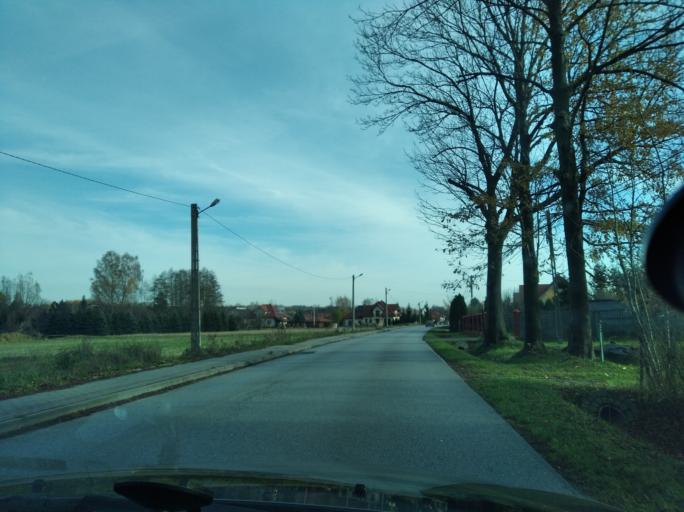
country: PL
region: Subcarpathian Voivodeship
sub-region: Powiat lancucki
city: Kraczkowa
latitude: 50.0376
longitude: 22.1496
